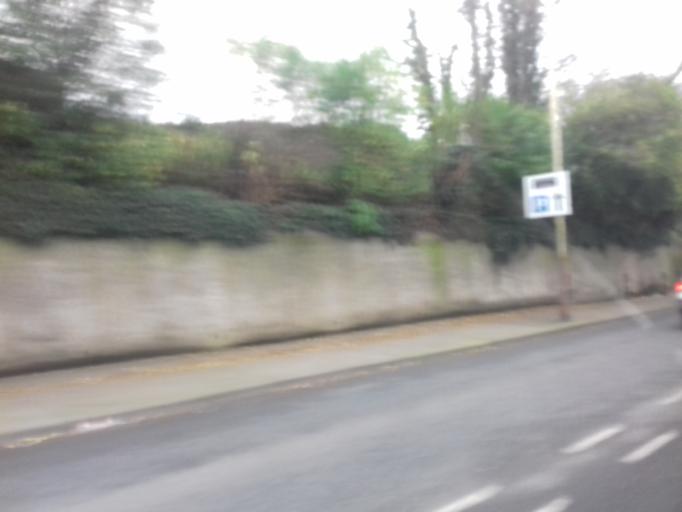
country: IE
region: Leinster
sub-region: Lu
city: Drogheda
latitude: 53.7128
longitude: -6.3391
